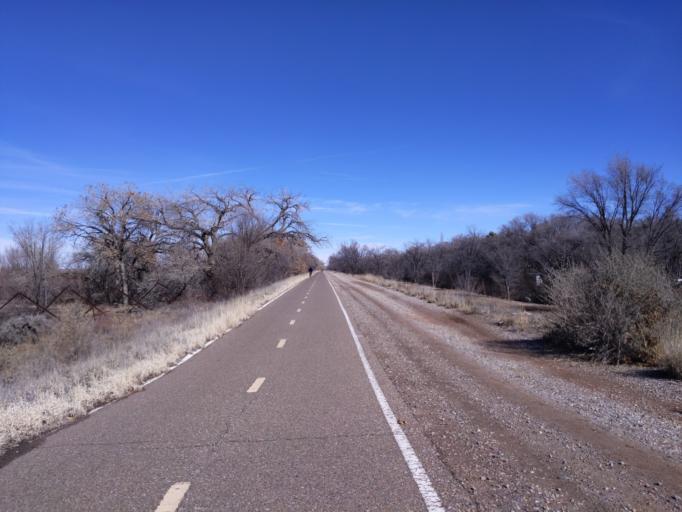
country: US
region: New Mexico
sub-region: Bernalillo County
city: Lee Acres
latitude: 35.1501
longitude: -106.6712
